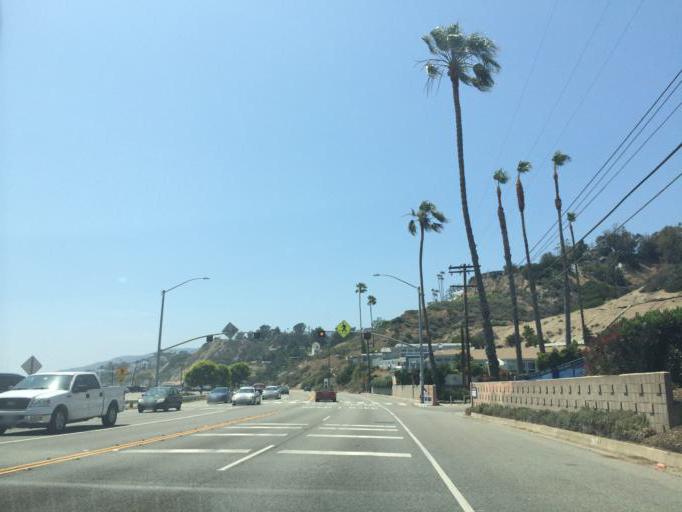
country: US
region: California
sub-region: Los Angeles County
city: Santa Monica
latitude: 34.0382
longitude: -118.5403
